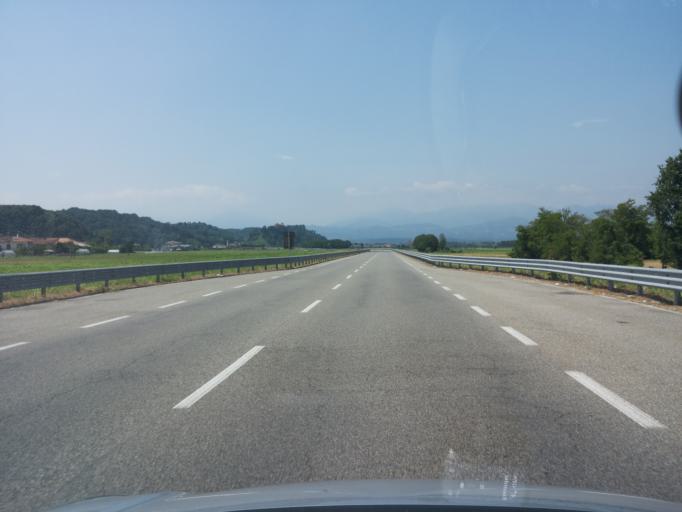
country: IT
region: Piedmont
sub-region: Provincia di Biella
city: Castelletto Cervo
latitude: 45.5210
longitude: 8.2044
